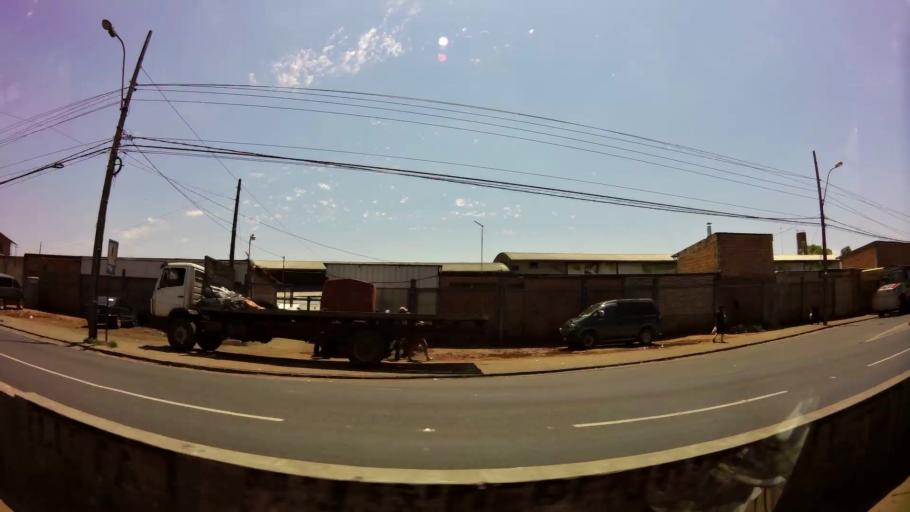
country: PY
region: Central
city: Lambare
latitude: -25.3282
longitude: -57.5707
